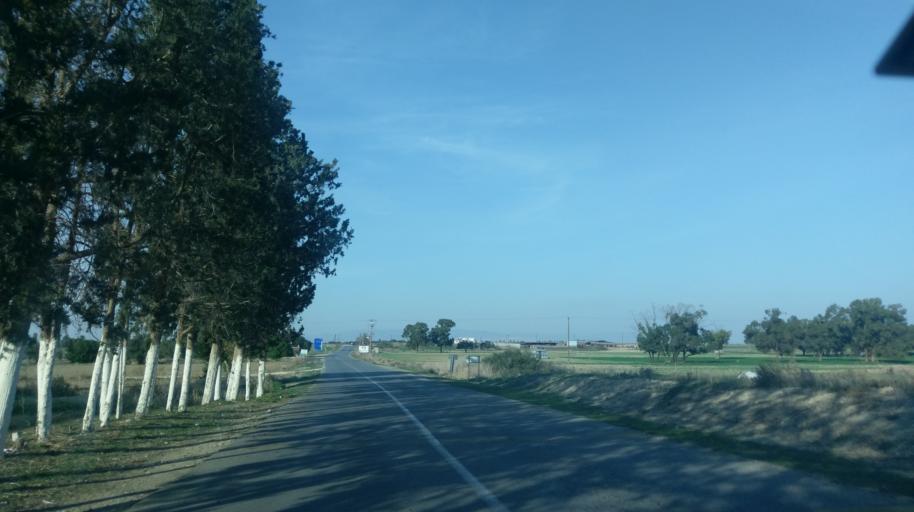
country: CY
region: Larnaka
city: Pergamos
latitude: 35.1104
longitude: 33.7278
